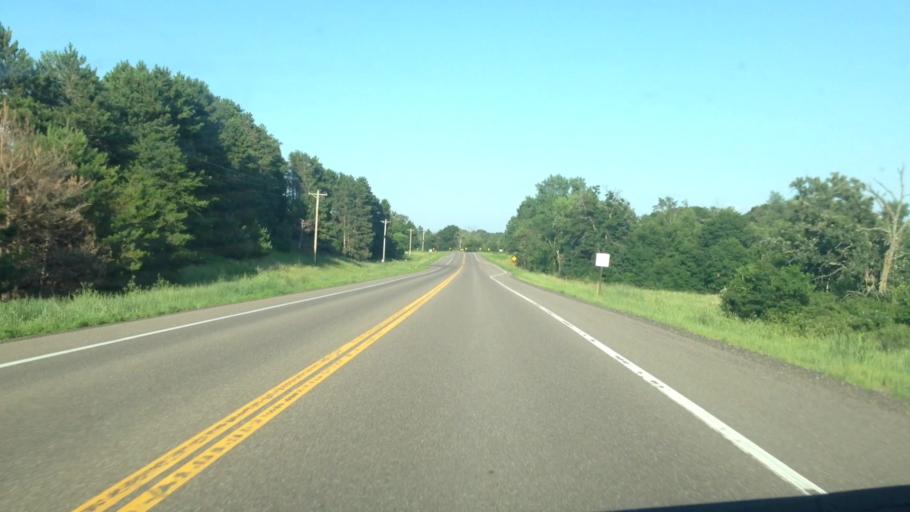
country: US
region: Minnesota
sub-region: Sherburne County
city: Zimmerman
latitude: 45.4437
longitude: -93.6496
